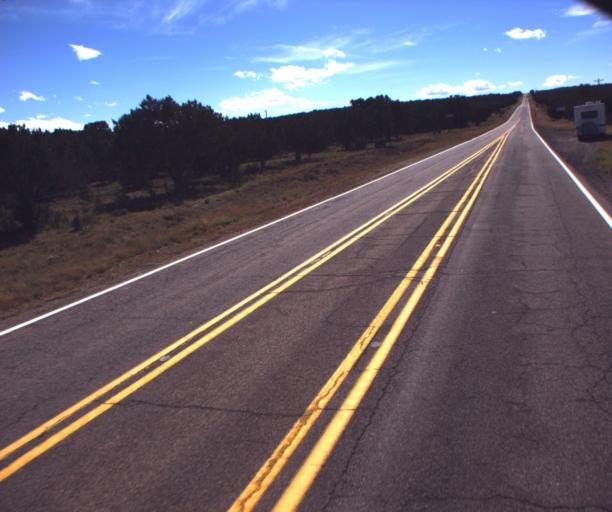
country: US
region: Arizona
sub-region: Navajo County
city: White Mountain Lake
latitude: 34.3027
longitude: -109.7860
